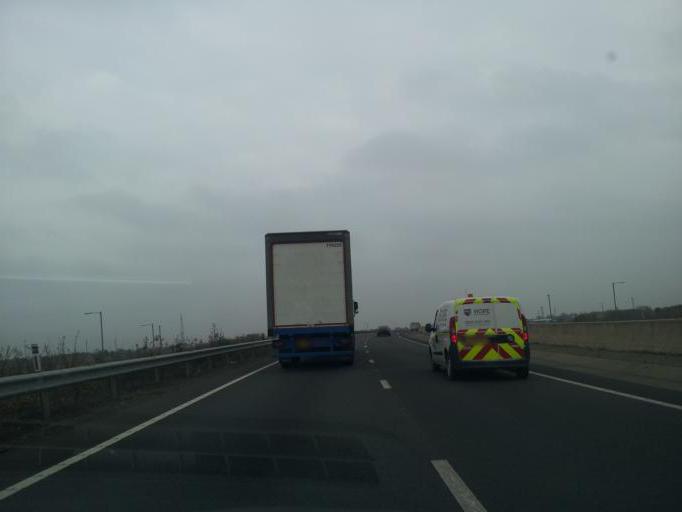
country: GB
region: England
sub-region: Bedford
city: Kempston
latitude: 52.1026
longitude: -0.5073
